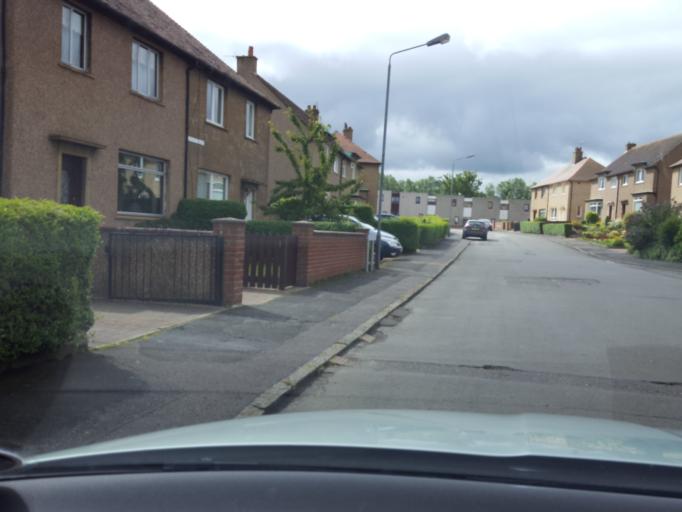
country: GB
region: Scotland
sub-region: Falkirk
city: Bo'ness
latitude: 56.0122
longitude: -3.5935
